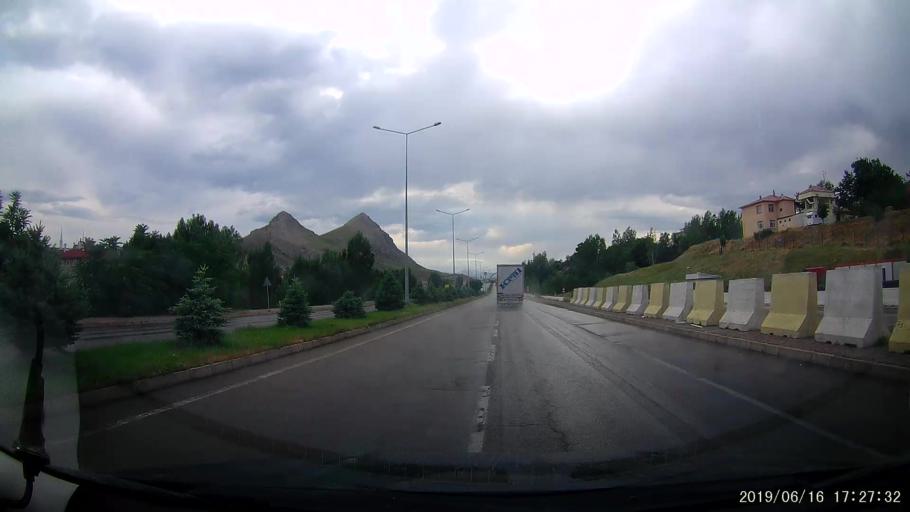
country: TR
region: Erzincan
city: Tercan
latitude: 39.7763
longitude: 40.3922
